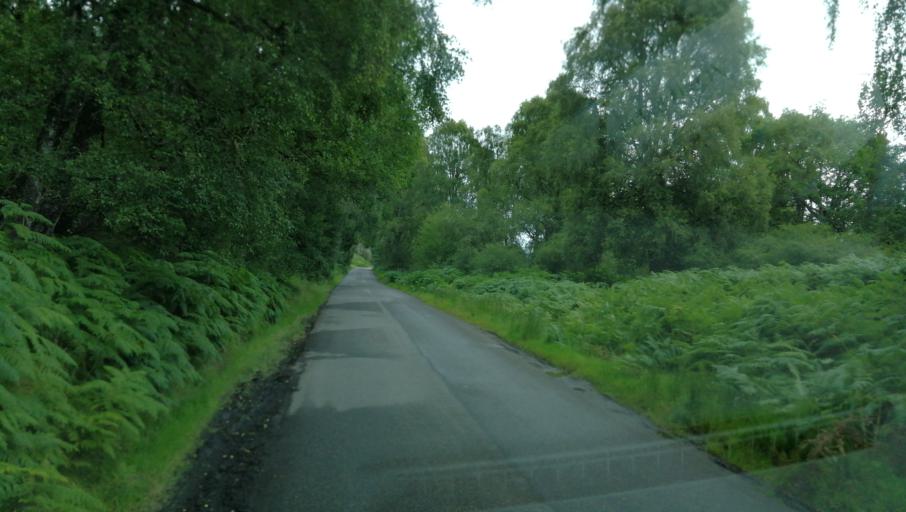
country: GB
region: Scotland
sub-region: Highland
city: Beauly
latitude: 57.3316
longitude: -4.7898
